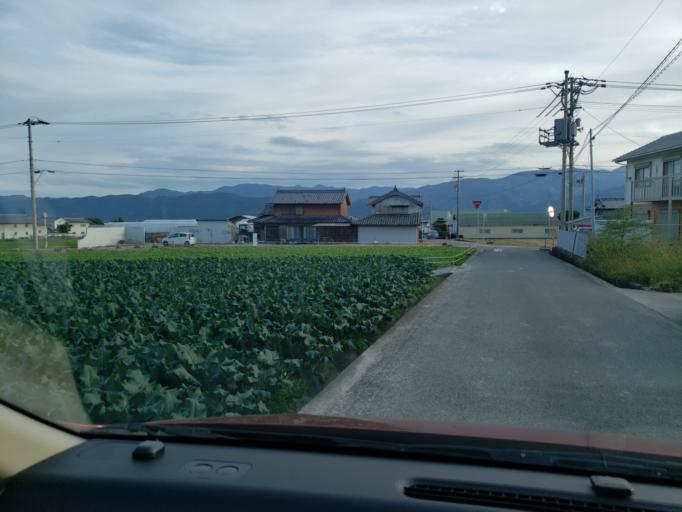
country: JP
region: Tokushima
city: Wakimachi
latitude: 34.0927
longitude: 134.2253
